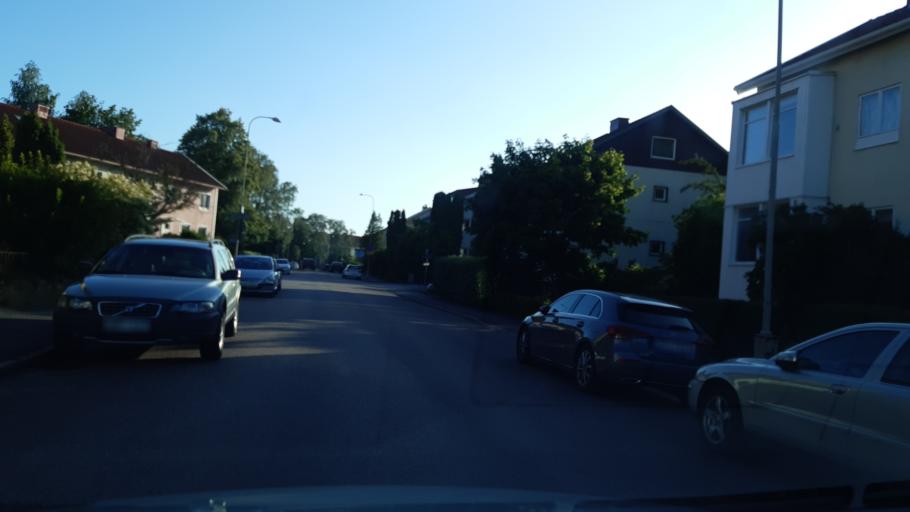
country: SE
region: Vaestra Goetaland
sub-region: Goteborg
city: Eriksbo
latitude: 57.7192
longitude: 12.0340
